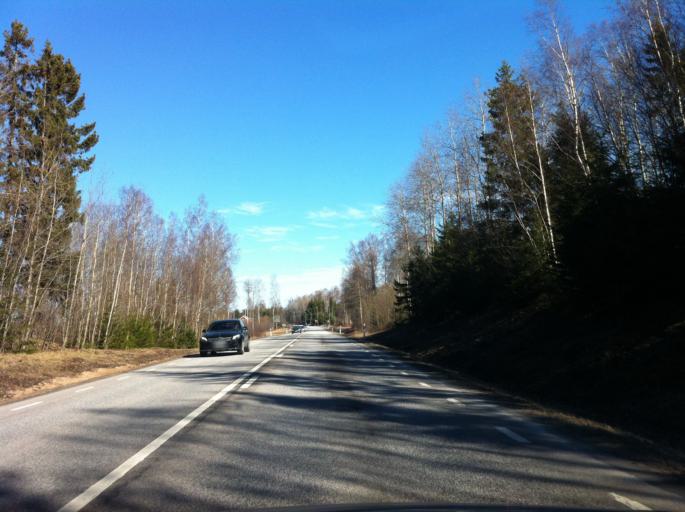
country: SE
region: Vaestra Goetaland
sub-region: Toreboda Kommun
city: Toereboda
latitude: 58.7972
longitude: 14.0909
